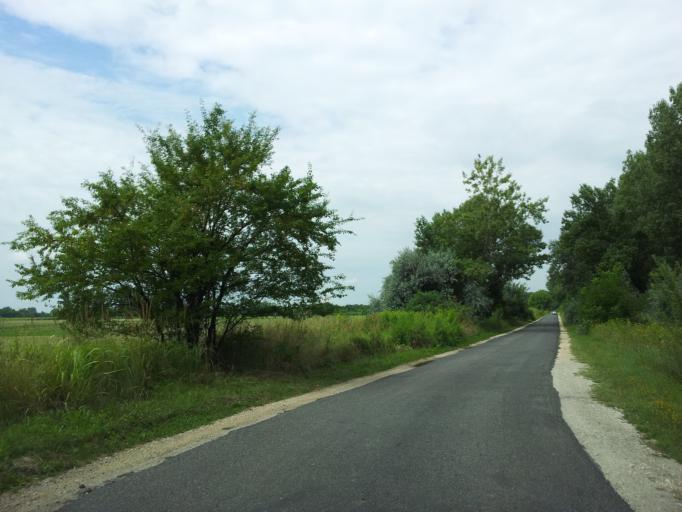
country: HU
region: Pest
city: Kiskunlachaza
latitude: 47.2322
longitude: 19.0069
